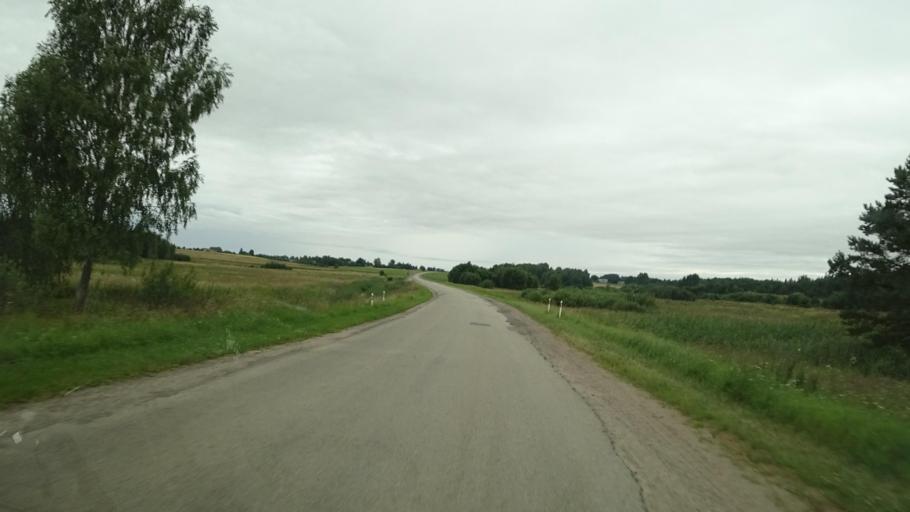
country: LT
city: Kelme
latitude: 55.4007
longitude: 22.8673
